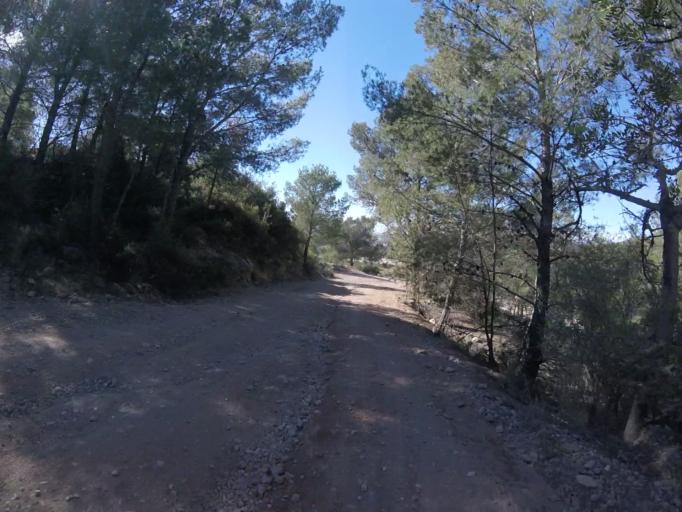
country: ES
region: Valencia
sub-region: Provincia de Castello
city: Benicassim
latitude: 40.0742
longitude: 0.0763
